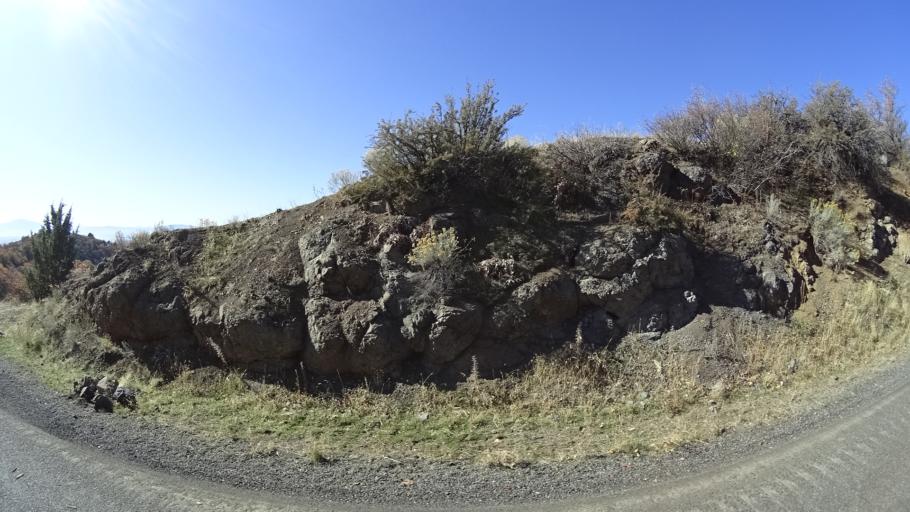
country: US
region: California
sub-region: Siskiyou County
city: Montague
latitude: 41.8306
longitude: -122.3324
